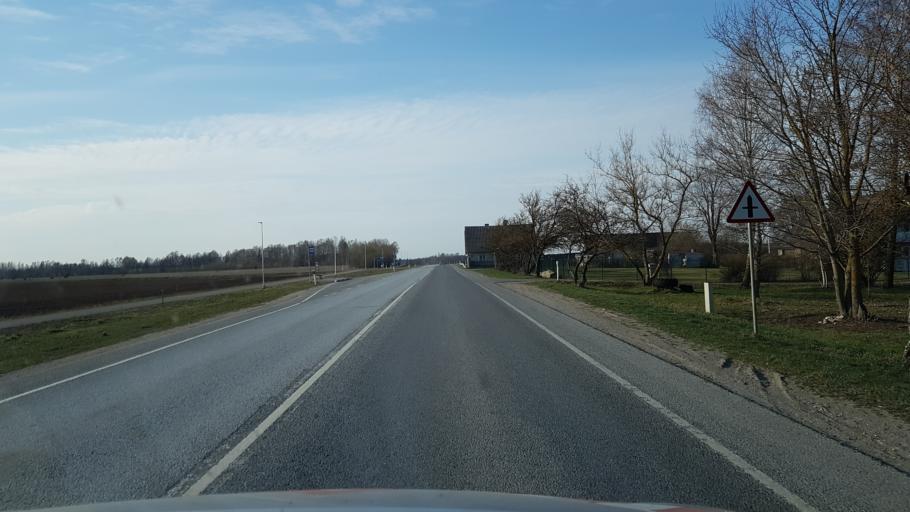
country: EE
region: Laeaene-Virumaa
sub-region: Rakvere linn
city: Rakvere
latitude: 59.3685
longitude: 26.3364
